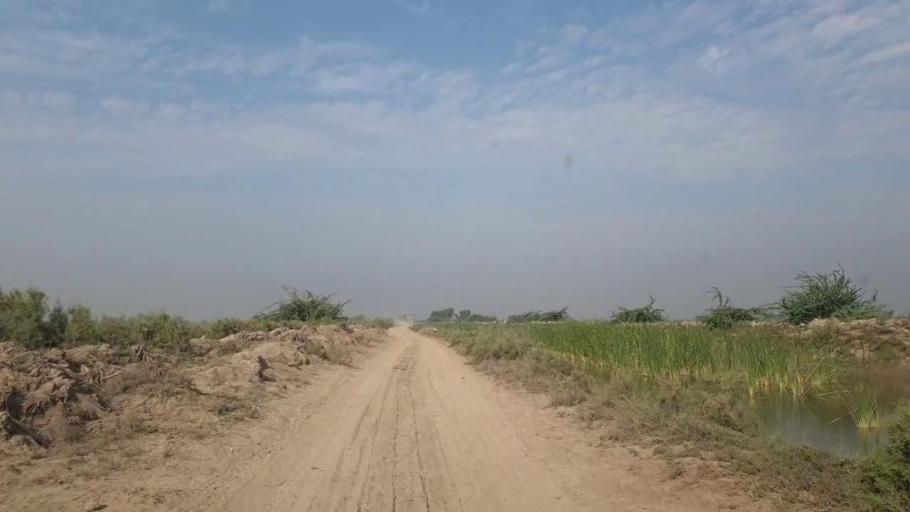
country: PK
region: Sindh
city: Tando Bago
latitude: 24.8733
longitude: 68.9639
